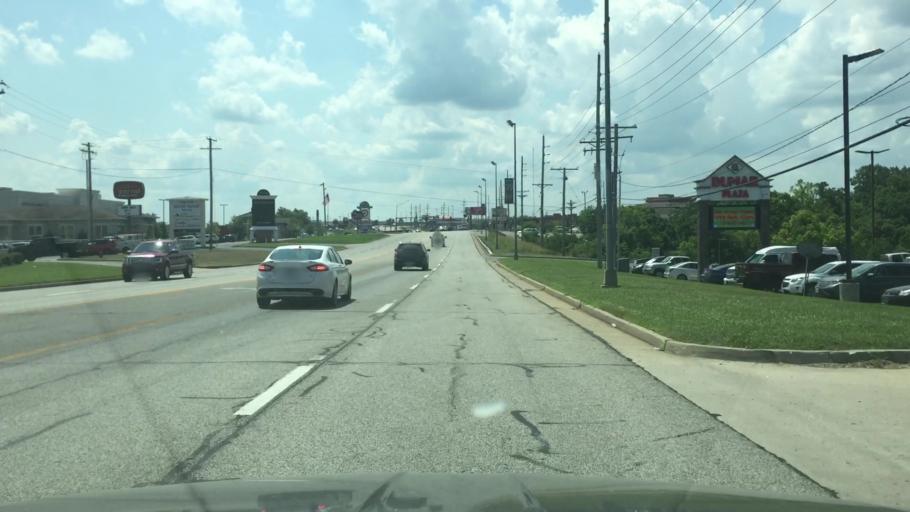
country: US
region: Missouri
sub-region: Miller County
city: Lake Ozark
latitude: 38.1645
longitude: -92.6096
